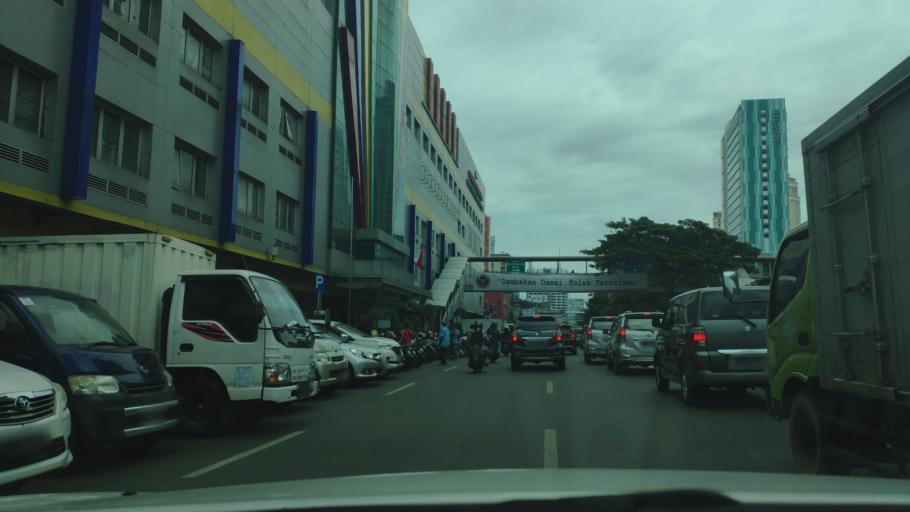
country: ID
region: Jakarta Raya
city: Jakarta
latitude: -6.1444
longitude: 106.8155
